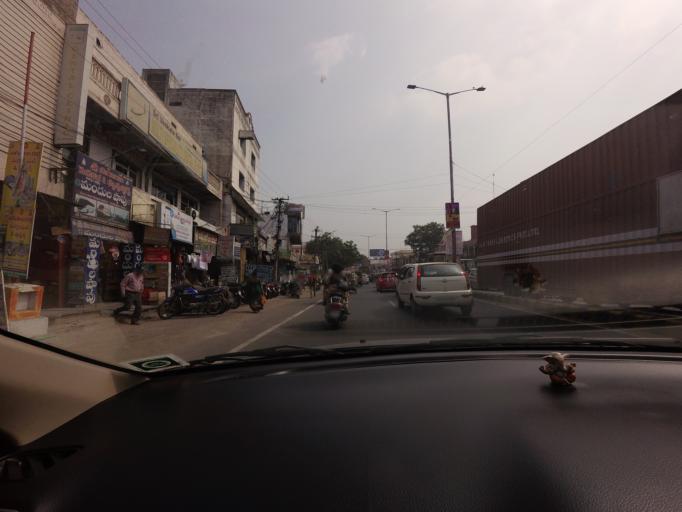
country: IN
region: Andhra Pradesh
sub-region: Krishna
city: Yanamalakuduru
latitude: 16.4960
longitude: 80.6595
